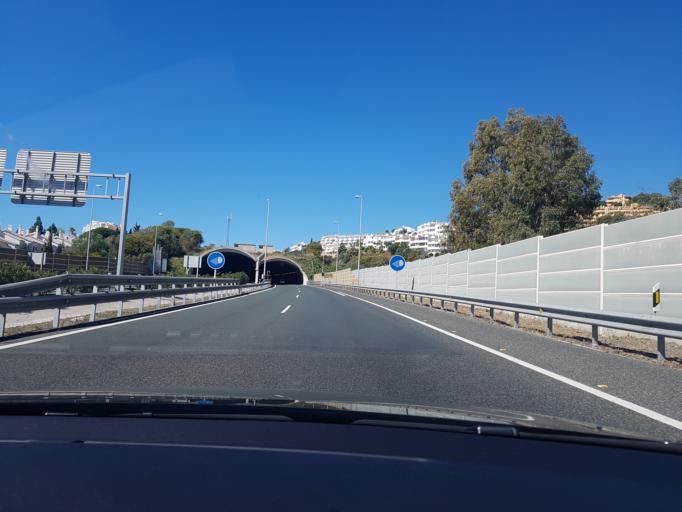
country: ES
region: Andalusia
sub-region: Provincia de Malaga
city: Fuengirola
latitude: 36.5069
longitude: -4.7228
